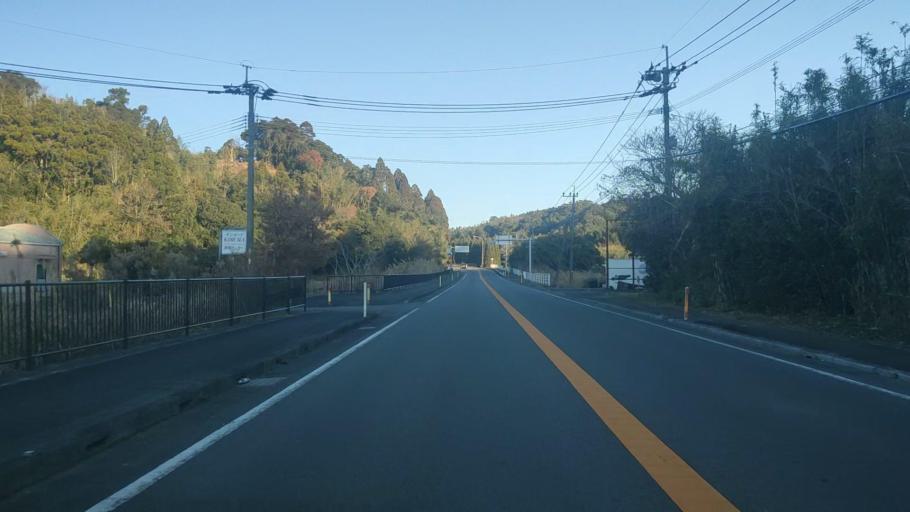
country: JP
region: Miyazaki
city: Takanabe
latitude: 32.1480
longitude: 131.5253
